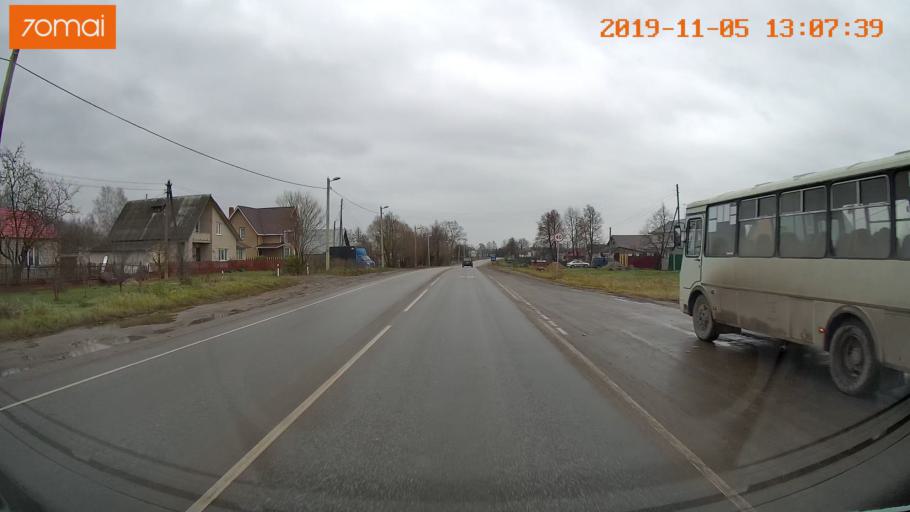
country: RU
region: Ivanovo
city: Kitovo
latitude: 56.8668
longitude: 41.2833
